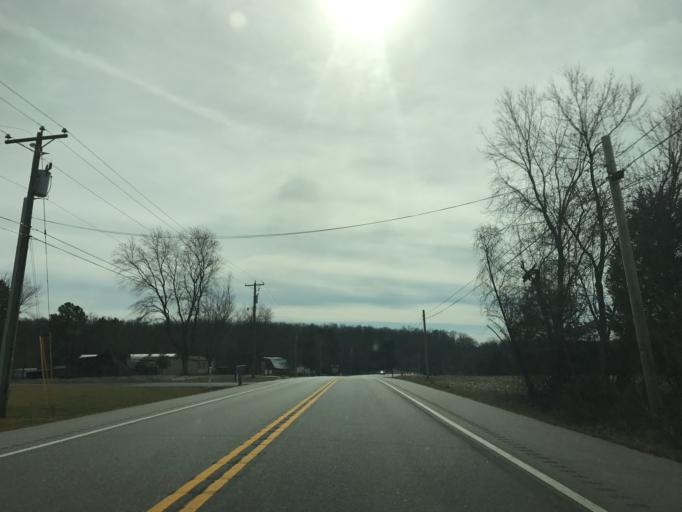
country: US
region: Maryland
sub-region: Queen Anne's County
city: Centreville
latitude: 39.1112
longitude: -76.0245
